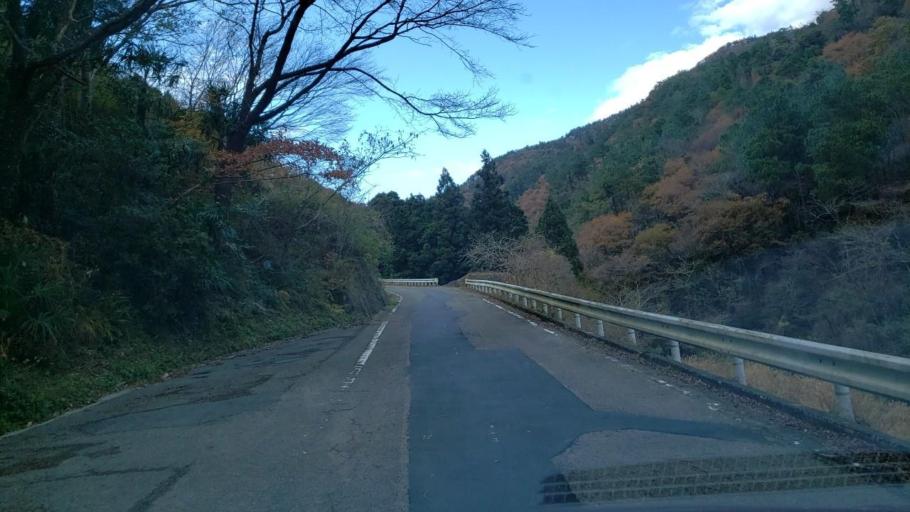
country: JP
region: Tokushima
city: Wakimachi
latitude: 34.1493
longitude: 134.2279
